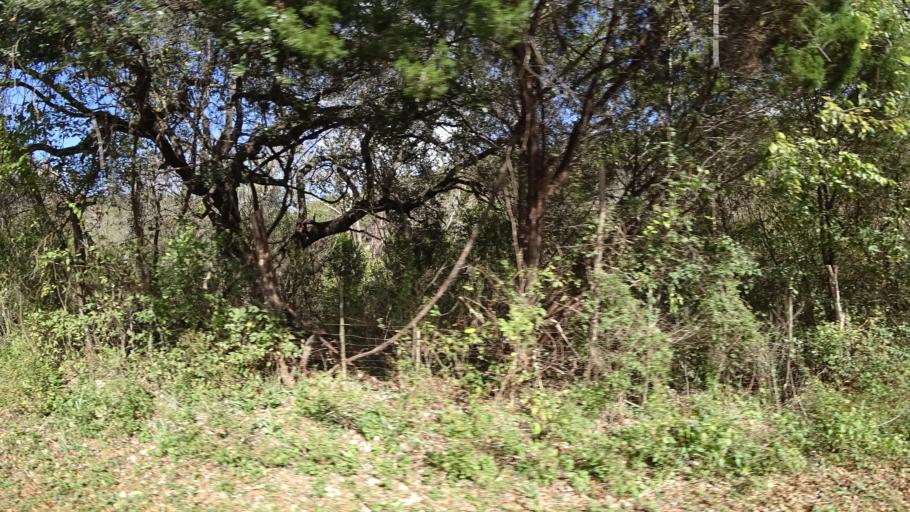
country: US
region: Texas
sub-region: Williamson County
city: Jollyville
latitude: 30.4039
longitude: -97.7859
